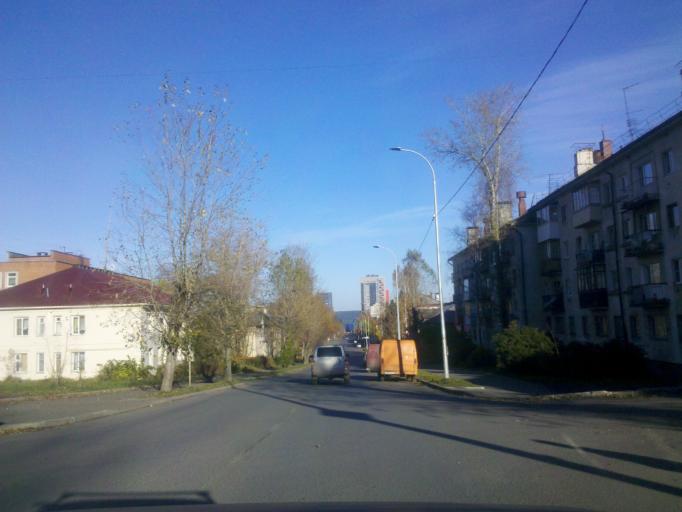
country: RU
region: Republic of Karelia
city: Petrozavodsk
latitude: 61.8007
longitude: 34.3312
